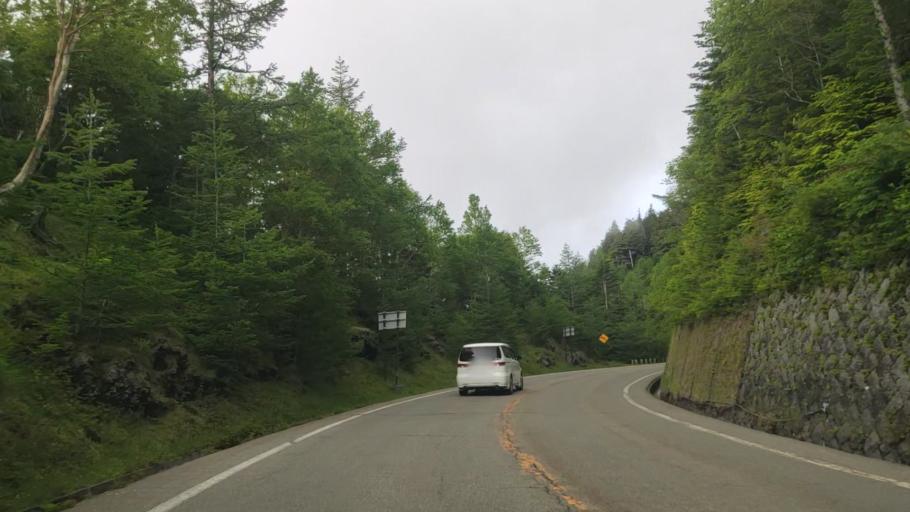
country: JP
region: Yamanashi
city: Fujikawaguchiko
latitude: 35.3831
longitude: 138.6948
